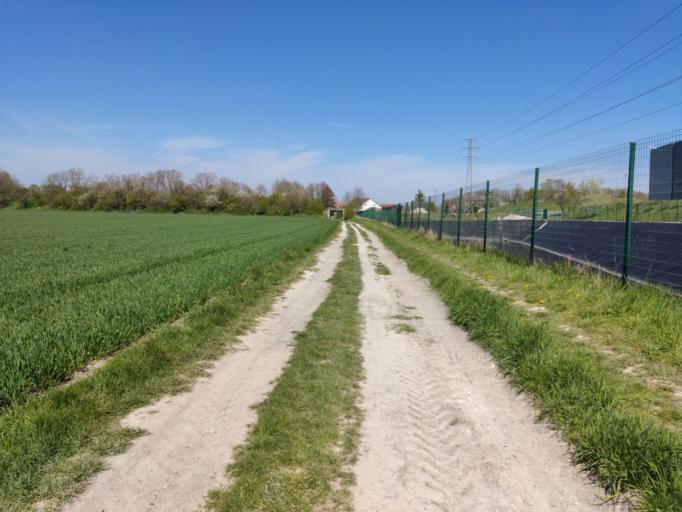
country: FR
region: Nord-Pas-de-Calais
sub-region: Departement du Pas-de-Calais
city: Henin-Beaumont
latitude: 50.3993
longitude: 2.9629
